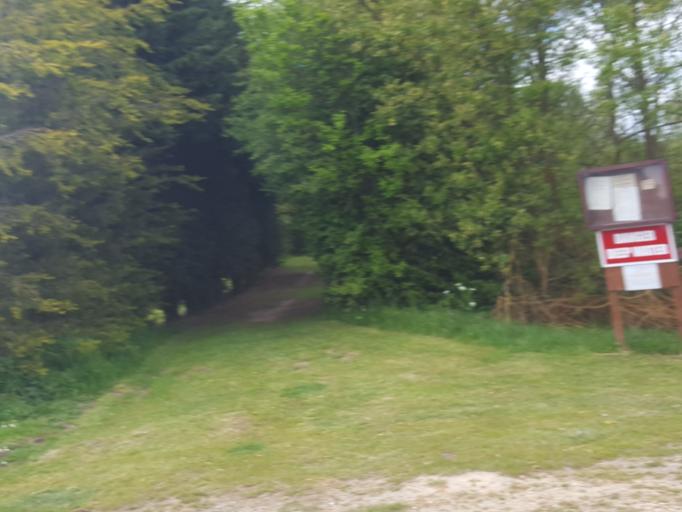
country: GB
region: England
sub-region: Essex
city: Frinton-on-Sea
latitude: 51.8320
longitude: 1.2000
